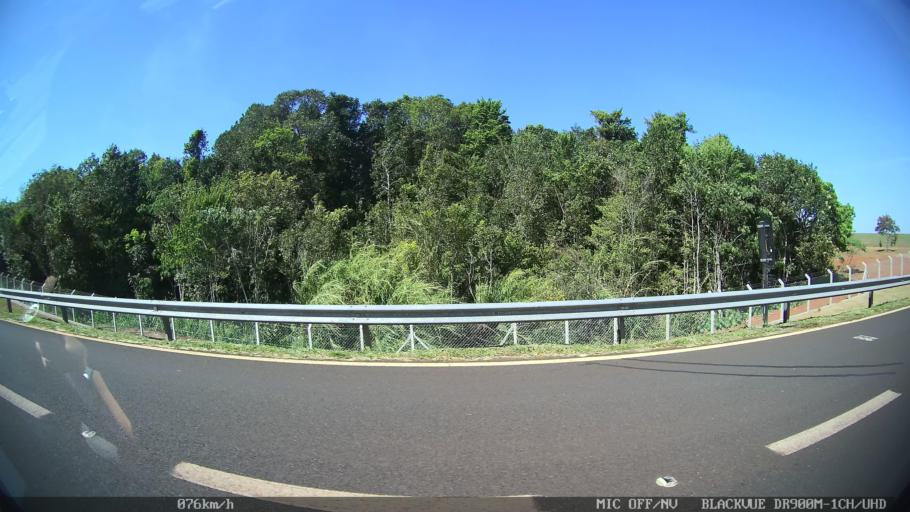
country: BR
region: Sao Paulo
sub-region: Batatais
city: Batatais
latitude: -20.8727
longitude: -47.6043
